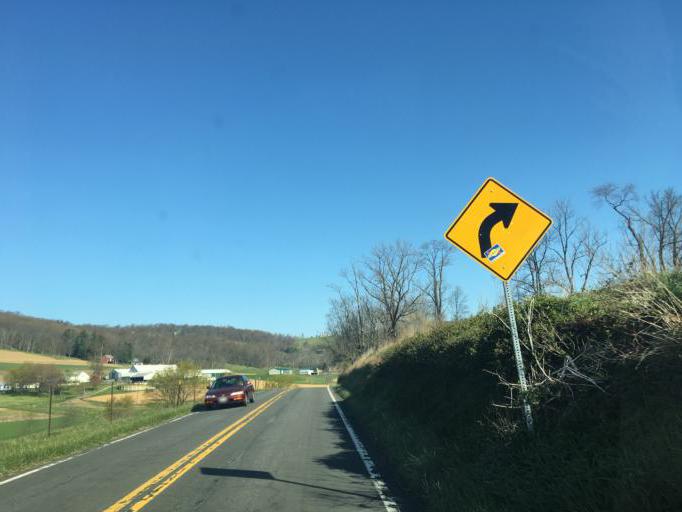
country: US
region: Maryland
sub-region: Frederick County
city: Myersville
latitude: 39.5358
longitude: -77.5436
